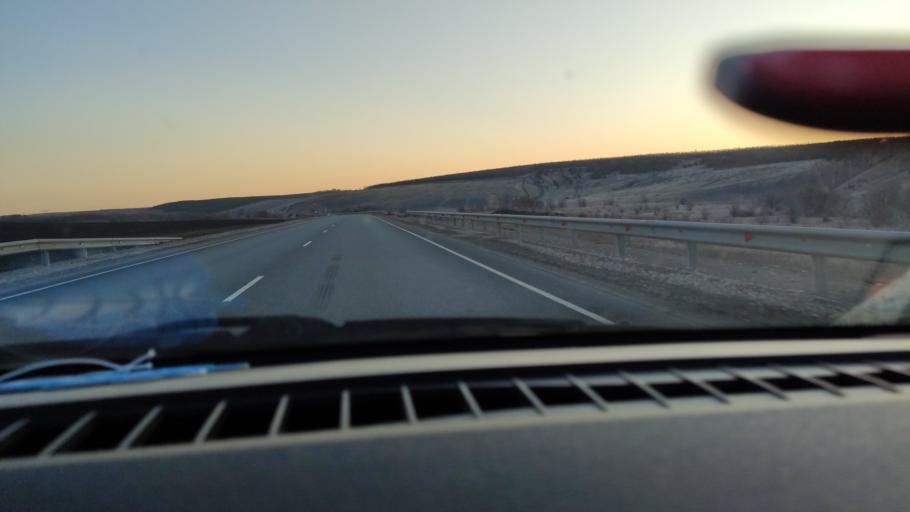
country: RU
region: Saratov
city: Yelshanka
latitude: 51.8625
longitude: 46.4996
